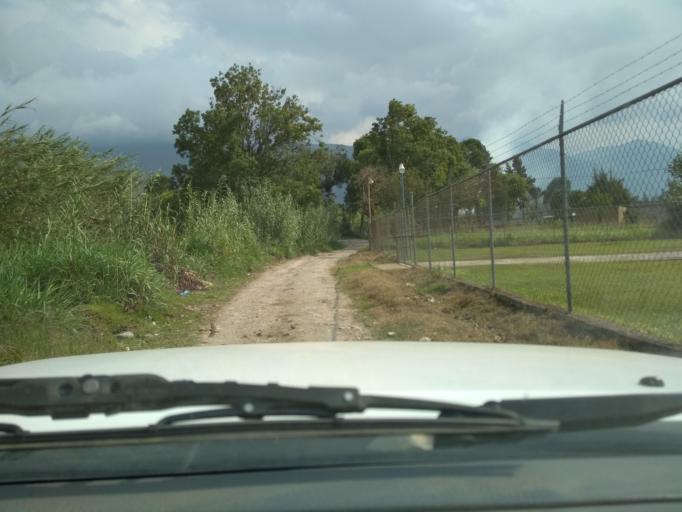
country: MX
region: Veracruz
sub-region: Acultzingo
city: Acatla
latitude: 18.7693
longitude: -97.2248
